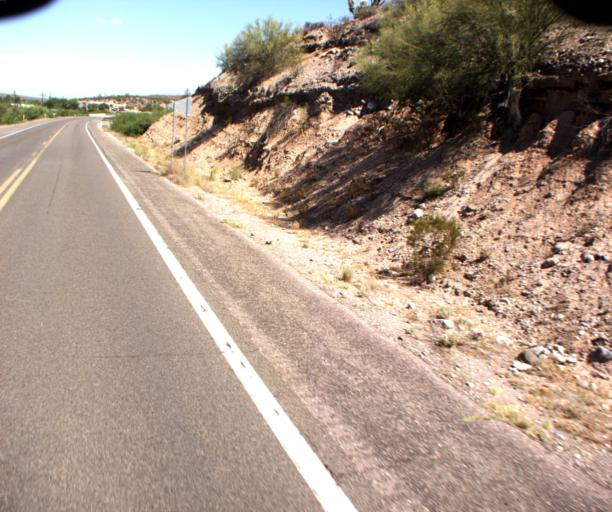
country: US
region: Arizona
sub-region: Pinal County
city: Kearny
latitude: 32.9294
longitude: -110.7318
